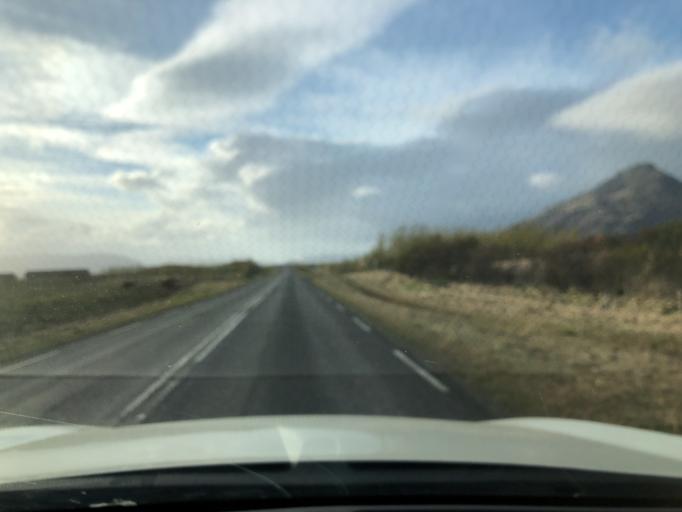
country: IS
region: East
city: Hoefn
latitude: 64.3016
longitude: -15.2032
